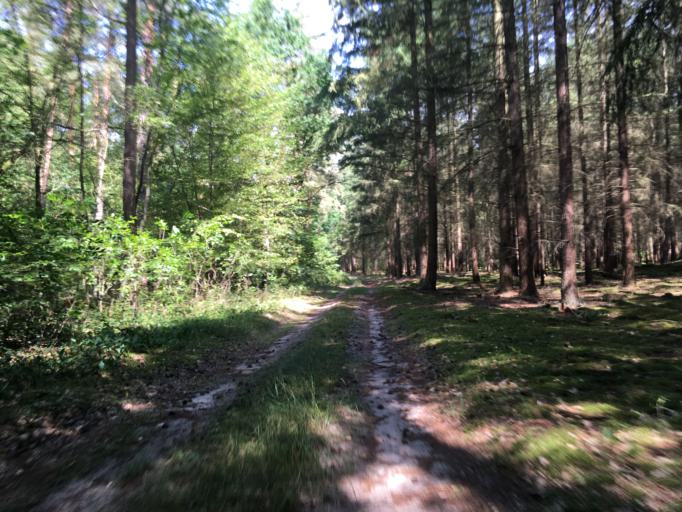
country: DE
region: Brandenburg
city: Casekow
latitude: 53.2341
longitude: 14.1198
